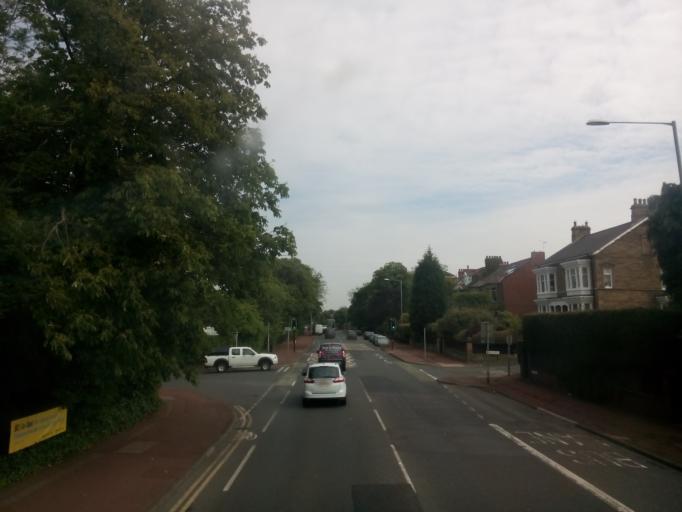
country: GB
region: England
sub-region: Gateshead
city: Gateshead
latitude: 54.9395
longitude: -1.5995
